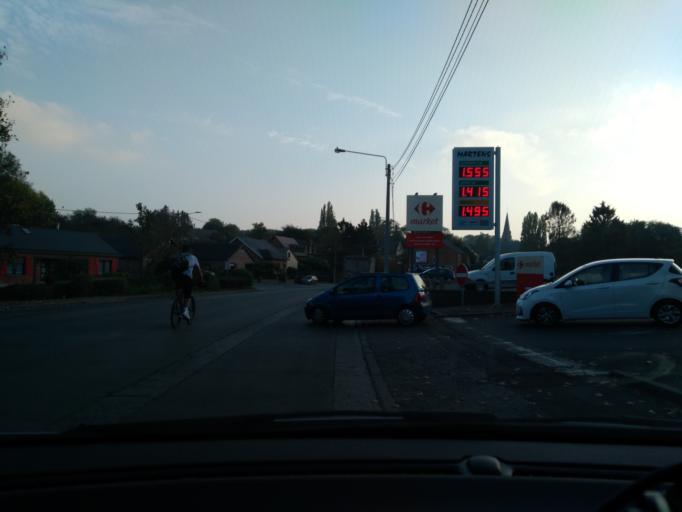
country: BE
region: Wallonia
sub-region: Province du Hainaut
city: Colfontaine
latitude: 50.4259
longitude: 3.8464
